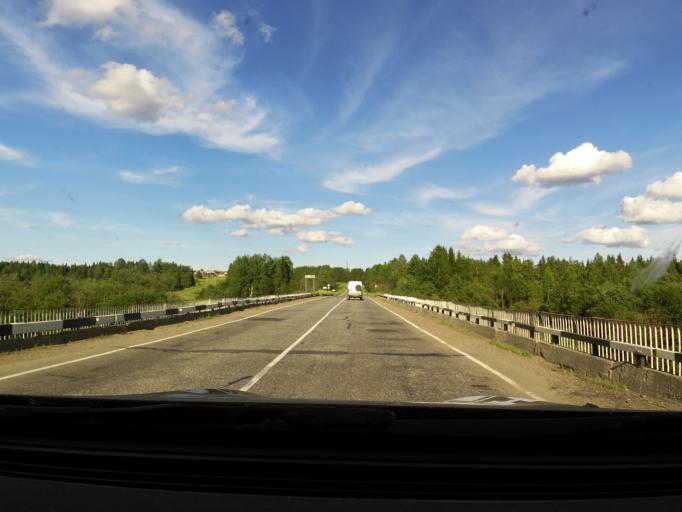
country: RU
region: Kirov
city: Belorechensk
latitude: 58.7129
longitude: 52.3153
